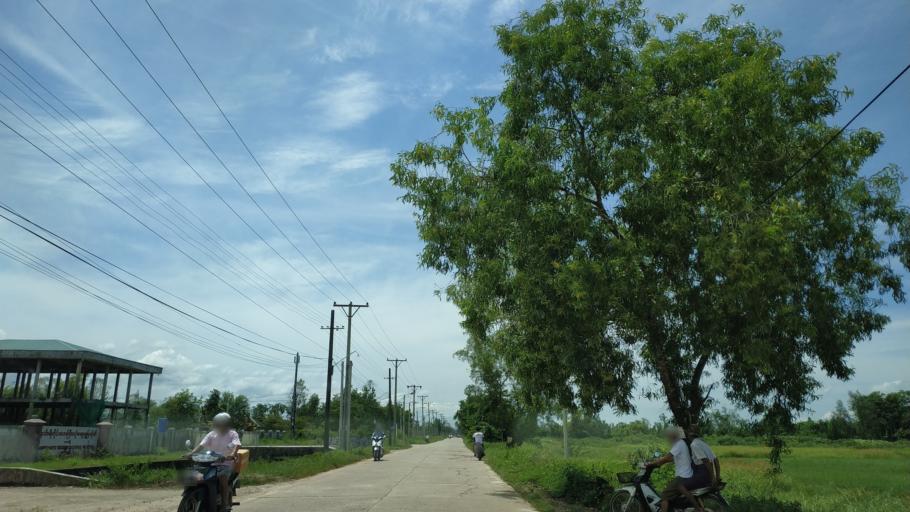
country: MM
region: Tanintharyi
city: Dawei
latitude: 14.0850
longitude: 98.1797
